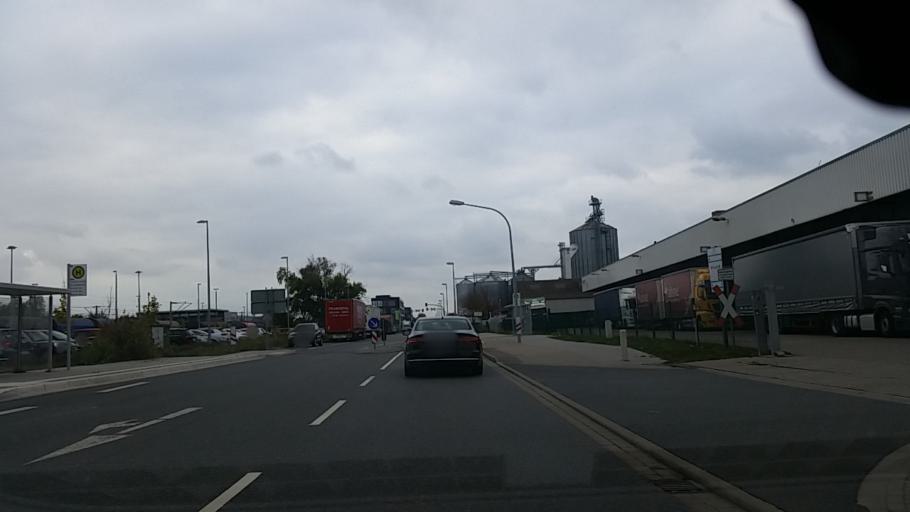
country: DE
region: Lower Saxony
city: Weyhausen
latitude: 52.4248
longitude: 10.7264
